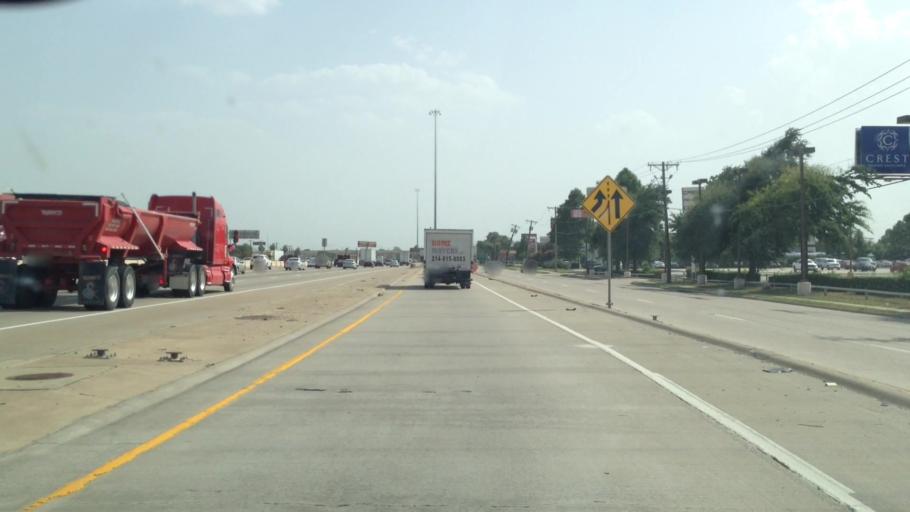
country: US
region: Texas
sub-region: Collin County
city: Plano
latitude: 33.0338
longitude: -96.7068
